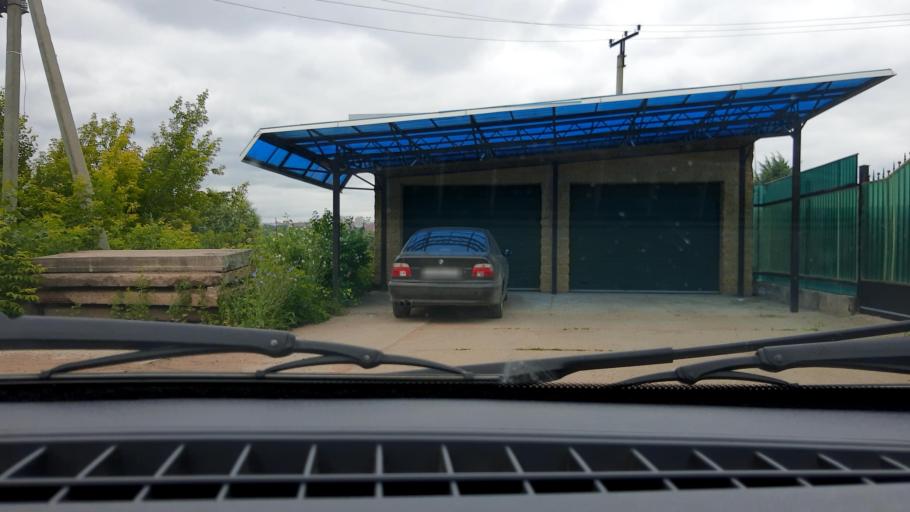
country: RU
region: Bashkortostan
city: Ufa
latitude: 54.7569
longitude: 55.9190
